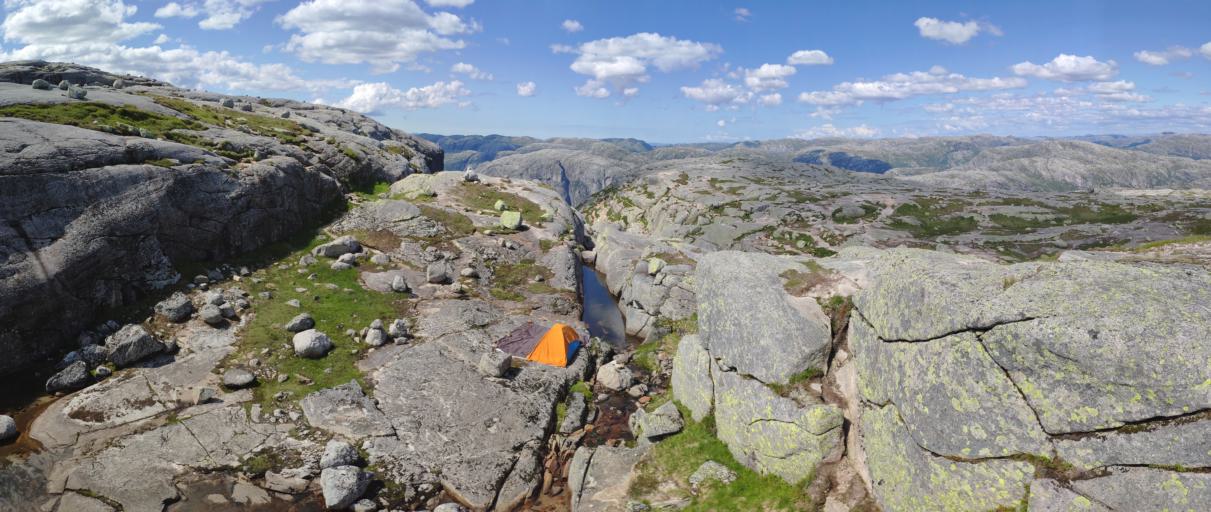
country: NO
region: Vest-Agder
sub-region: Sirdal
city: Tonstad
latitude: 59.0330
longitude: 6.5954
